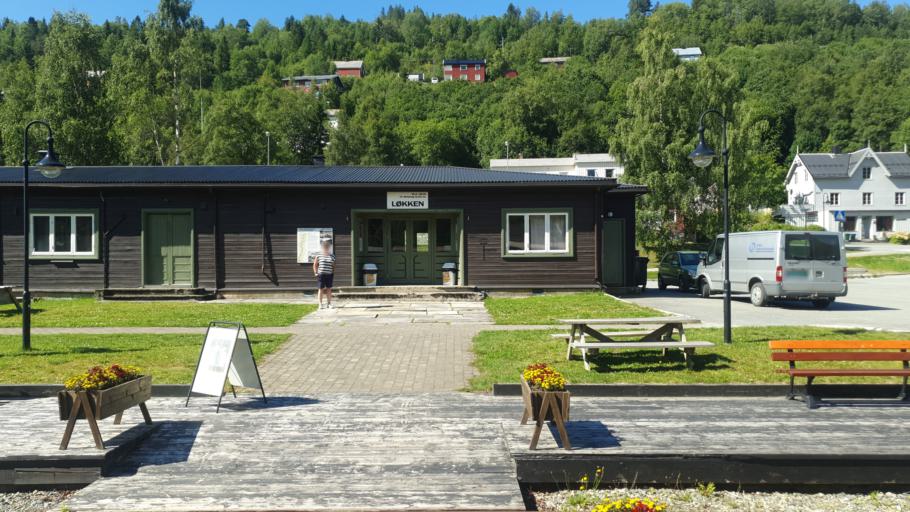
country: NO
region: Sor-Trondelag
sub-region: Meldal
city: Meldal
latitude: 63.1255
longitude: 9.7056
